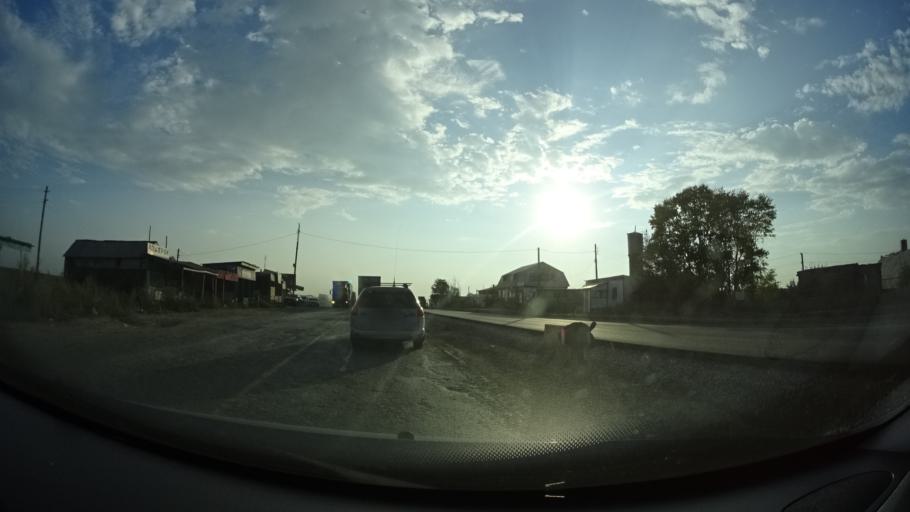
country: RU
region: Samara
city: Kamyshla
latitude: 54.0652
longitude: 52.1417
